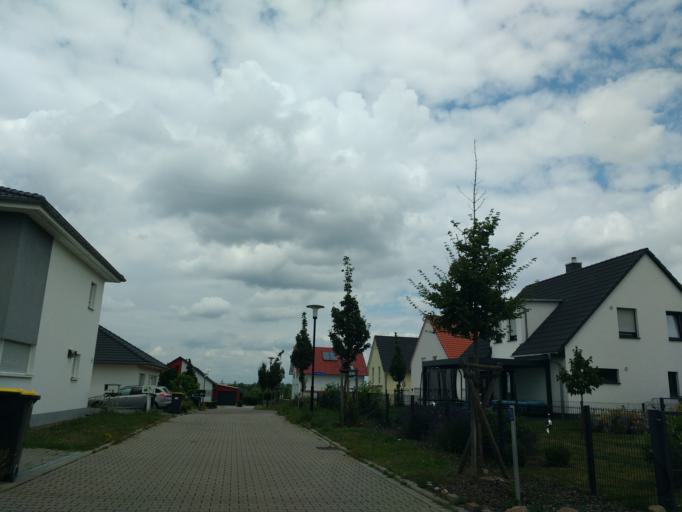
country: DE
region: Saxony-Anhalt
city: Angersdorf
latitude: 51.4417
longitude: 11.9347
